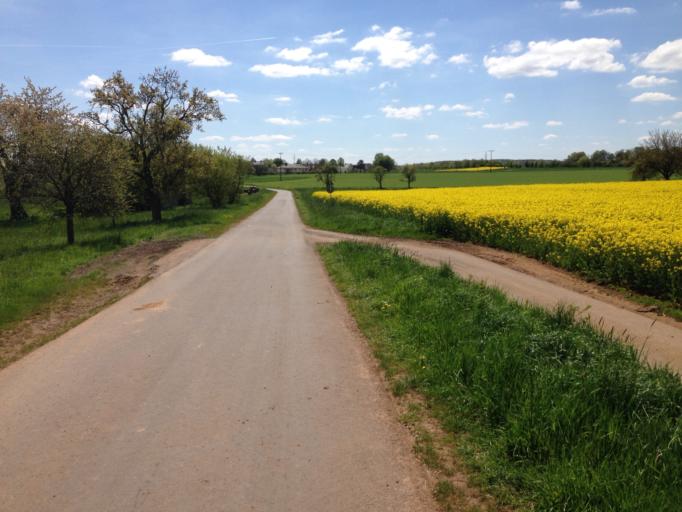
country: DE
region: Hesse
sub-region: Regierungsbezirk Giessen
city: Lich
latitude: 50.4998
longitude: 8.8517
